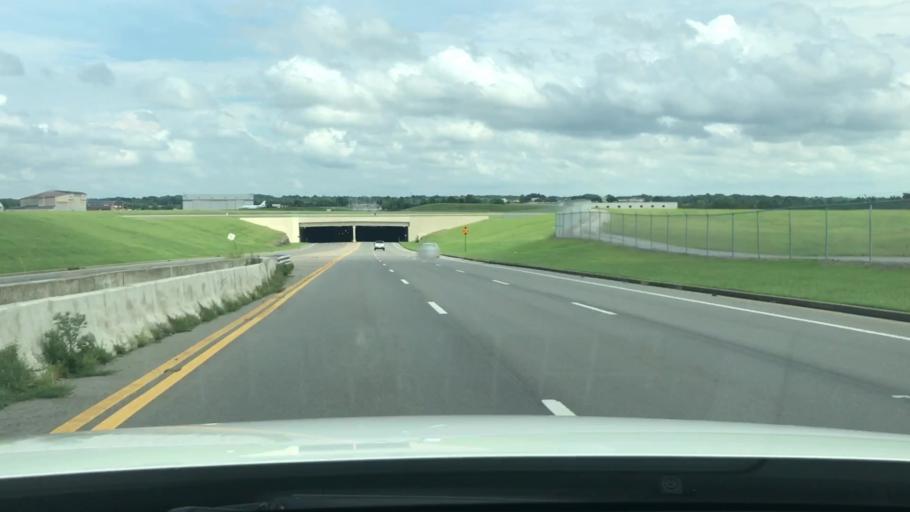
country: US
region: Tennessee
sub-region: Davidson County
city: Oak Hill
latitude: 36.1126
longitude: -86.6883
